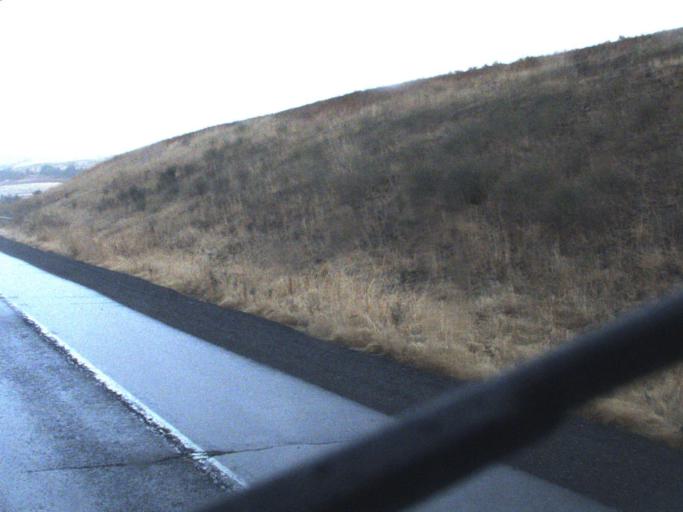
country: US
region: Washington
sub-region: Spokane County
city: Cheney
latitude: 47.2494
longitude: -117.3618
